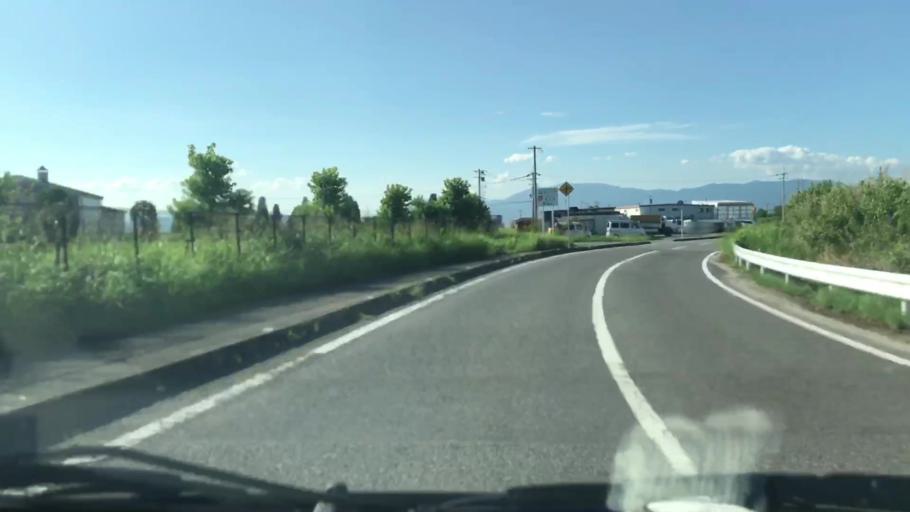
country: JP
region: Saga Prefecture
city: Okawa
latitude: 33.1868
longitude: 130.2901
